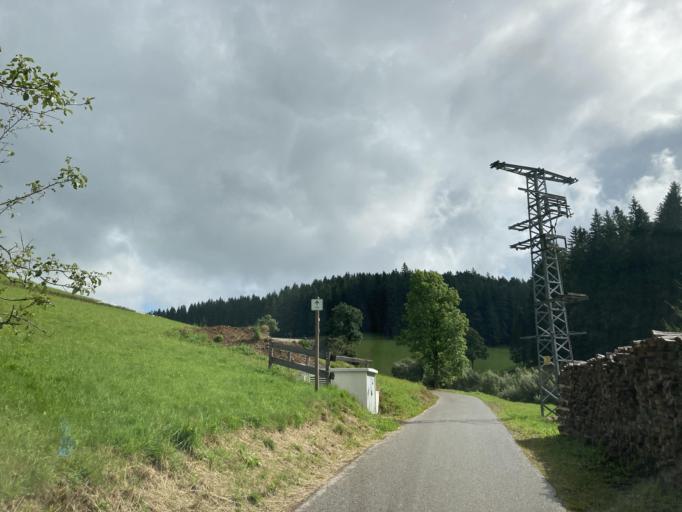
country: DE
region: Baden-Wuerttemberg
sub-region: Freiburg Region
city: Furtwangen im Schwarzwald
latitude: 48.0222
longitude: 8.1870
